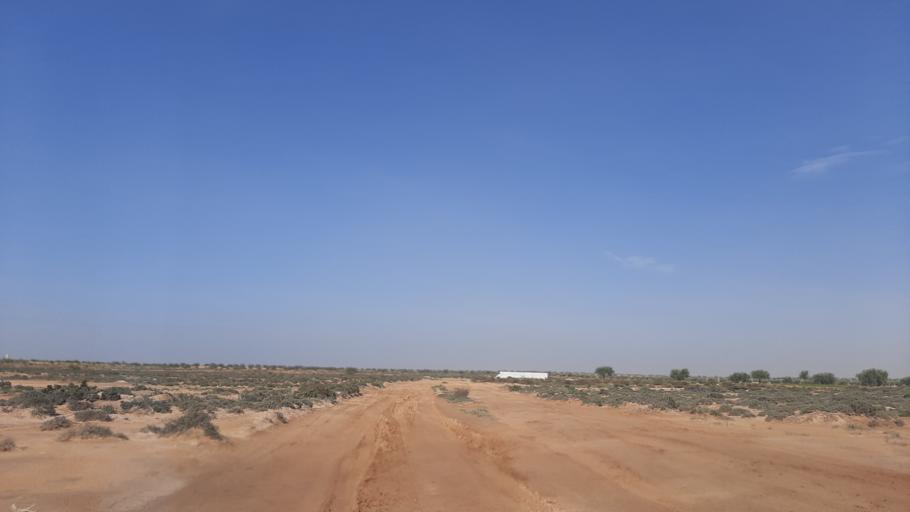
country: TN
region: Madanin
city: Zarzis
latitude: 33.4483
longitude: 10.8078
